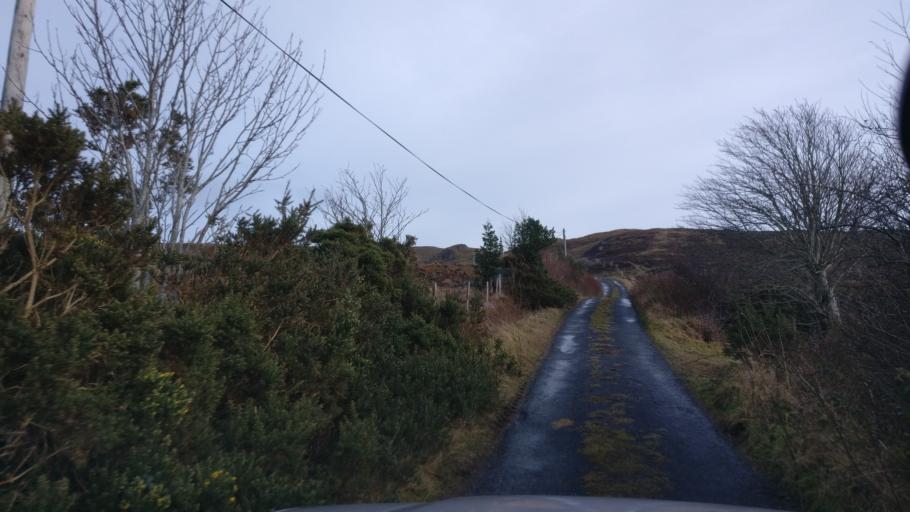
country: IE
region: Connaught
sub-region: County Galway
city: Oughterard
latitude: 53.5518
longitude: -9.4384
